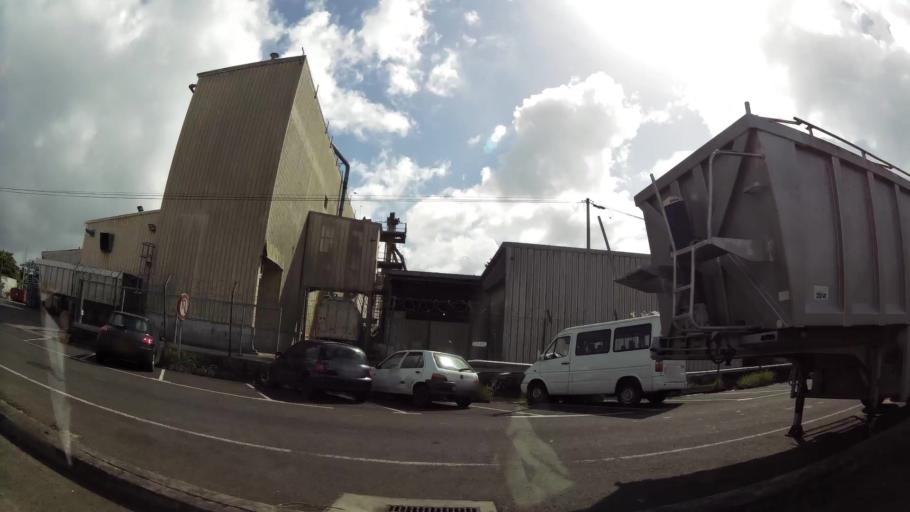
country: MQ
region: Martinique
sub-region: Martinique
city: Fort-de-France
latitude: 14.5963
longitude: -61.0560
